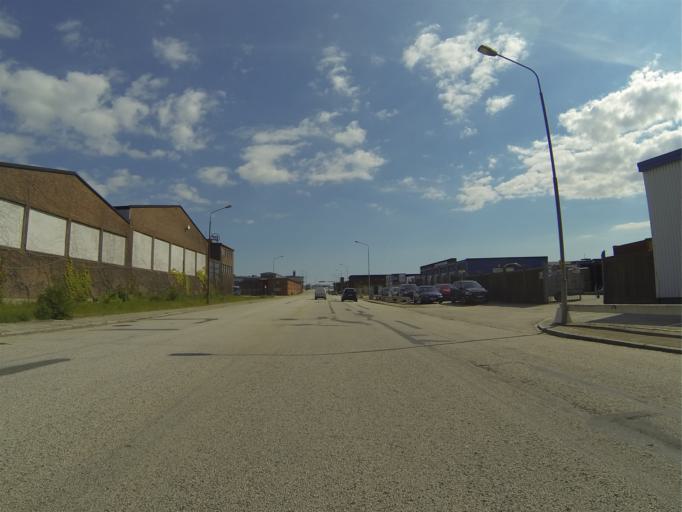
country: SE
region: Skane
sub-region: Malmo
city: Malmoe
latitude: 55.6177
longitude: 13.0199
